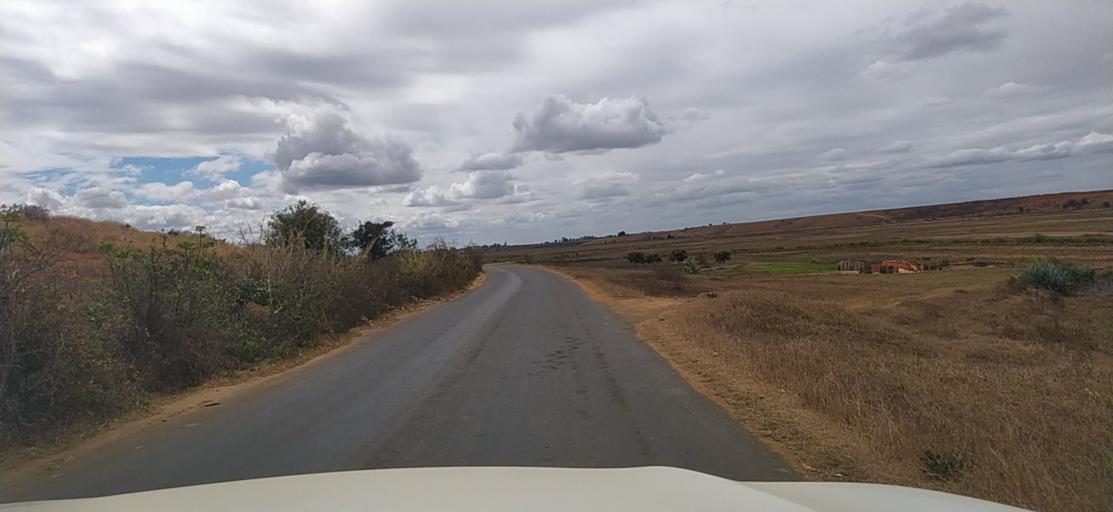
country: MG
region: Alaotra Mangoro
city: Ambatondrazaka
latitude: -17.9244
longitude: 48.2582
